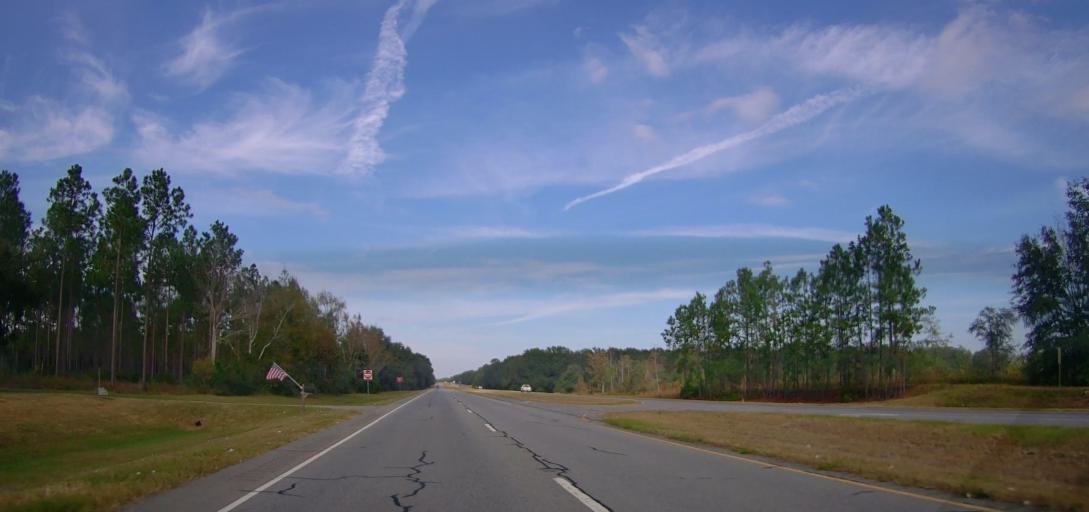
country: US
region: Georgia
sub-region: Mitchell County
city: Camilla
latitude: 31.2947
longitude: -84.1836
